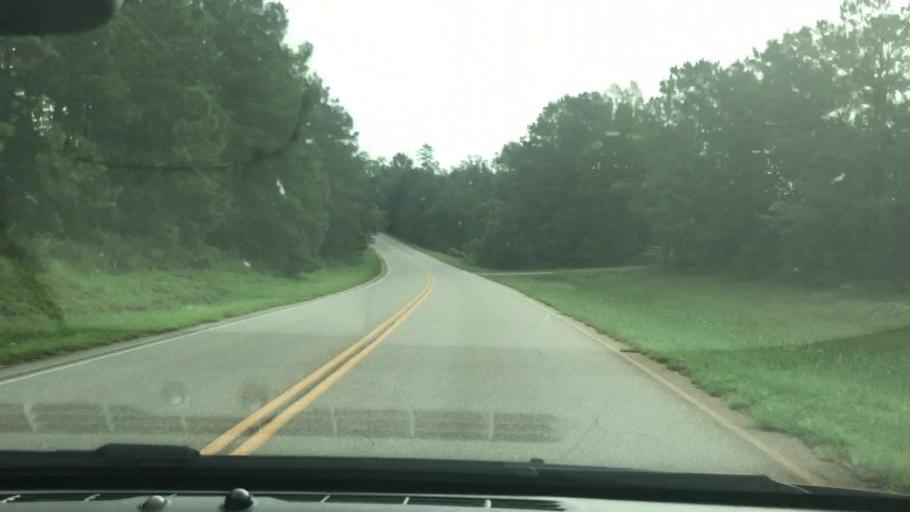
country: US
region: Georgia
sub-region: Stewart County
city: Lumpkin
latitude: 31.9799
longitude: -84.9427
